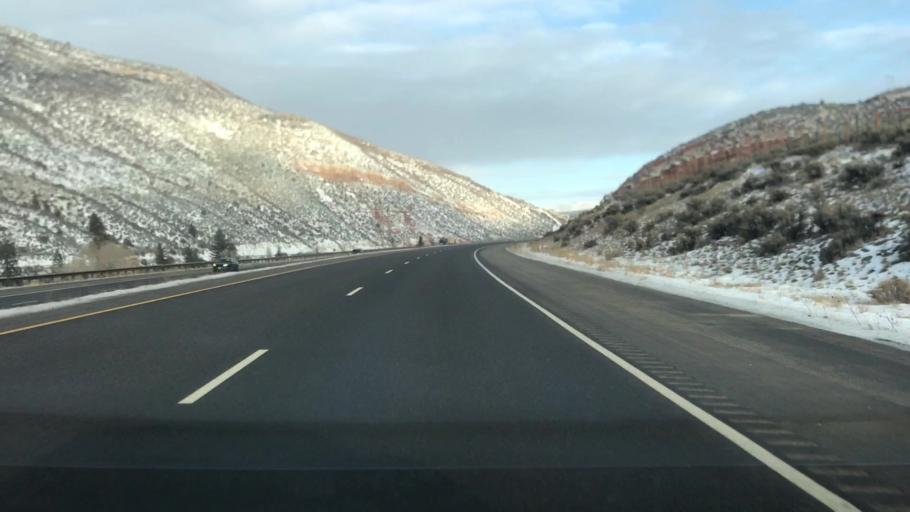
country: US
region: Colorado
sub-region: Eagle County
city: Edwards
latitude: 39.6639
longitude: -106.6422
